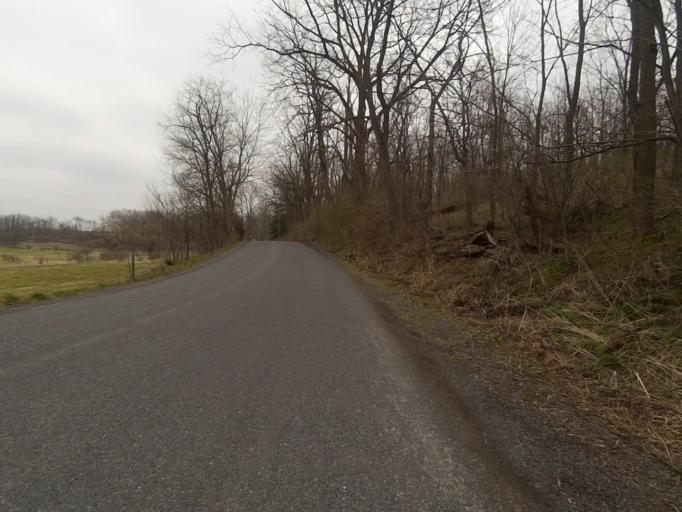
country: US
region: Pennsylvania
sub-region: Centre County
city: Boalsburg
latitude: 40.7911
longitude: -77.7788
